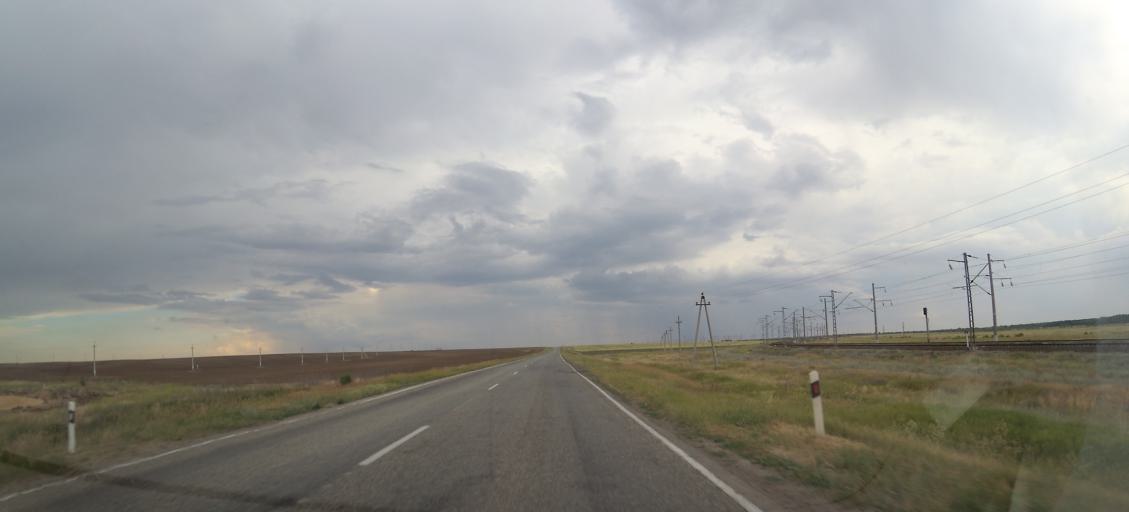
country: RU
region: Rostov
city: Dubovskoye
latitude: 47.4321
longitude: 42.7772
